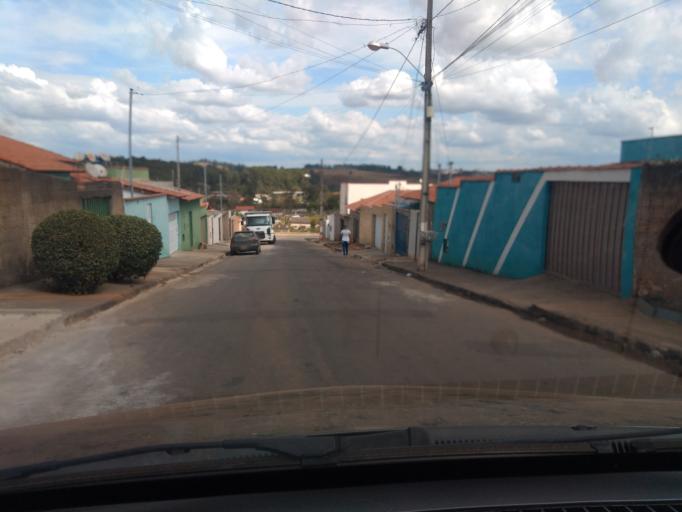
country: BR
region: Minas Gerais
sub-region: Tres Coracoes
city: Tres Coracoes
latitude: -21.6966
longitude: -45.2411
